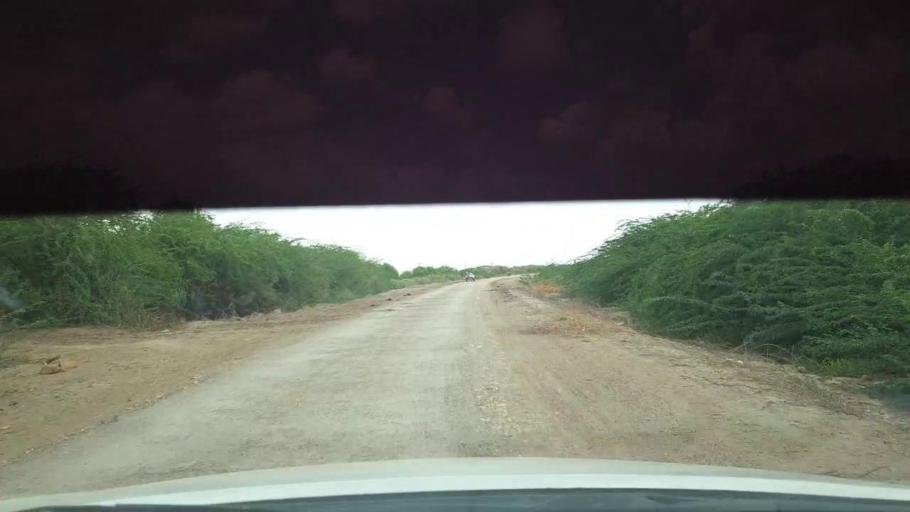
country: PK
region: Sindh
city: Kadhan
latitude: 24.4685
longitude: 69.0503
